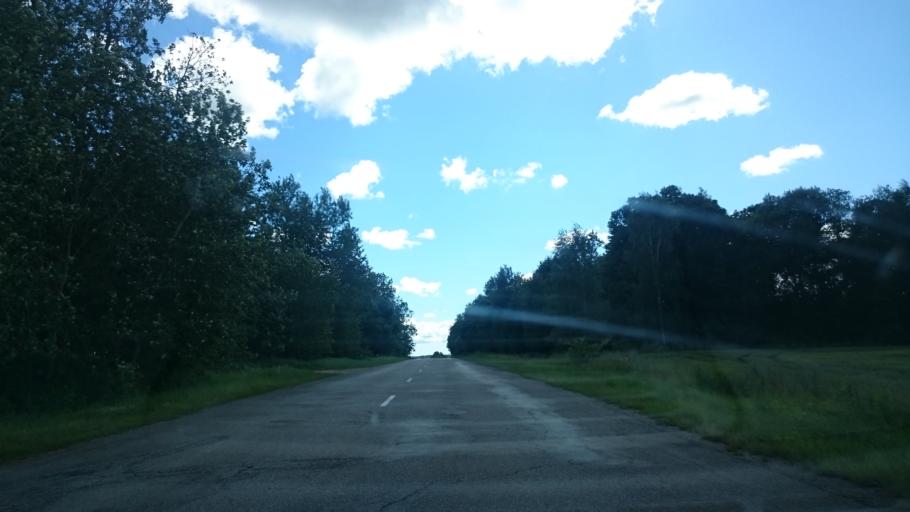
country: LV
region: Aizpute
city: Aizpute
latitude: 56.8324
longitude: 21.7511
